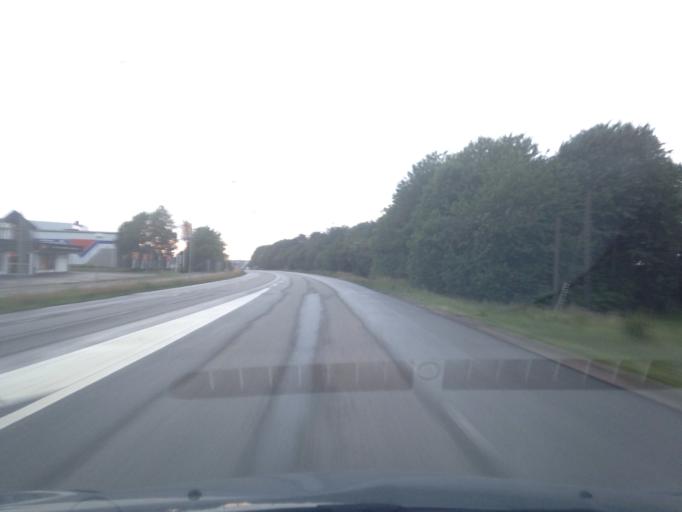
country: SE
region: Halland
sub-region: Varbergs Kommun
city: Varberg
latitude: 57.1239
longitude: 12.2748
